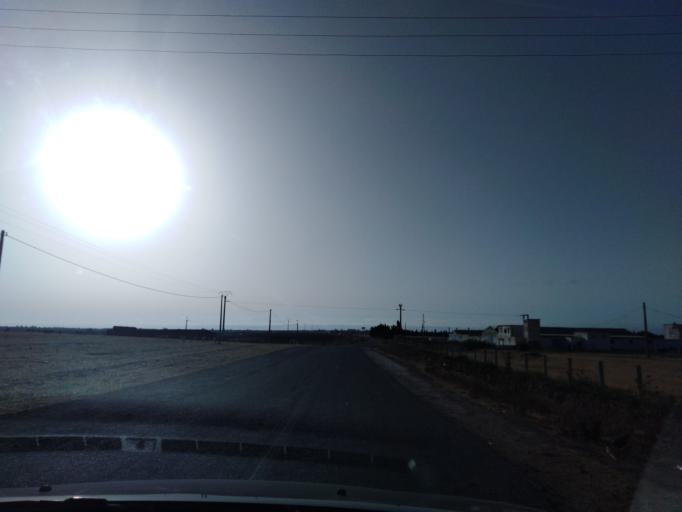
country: MA
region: Doukkala-Abda
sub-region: Safi
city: Safi
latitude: 32.4880
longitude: -8.9207
